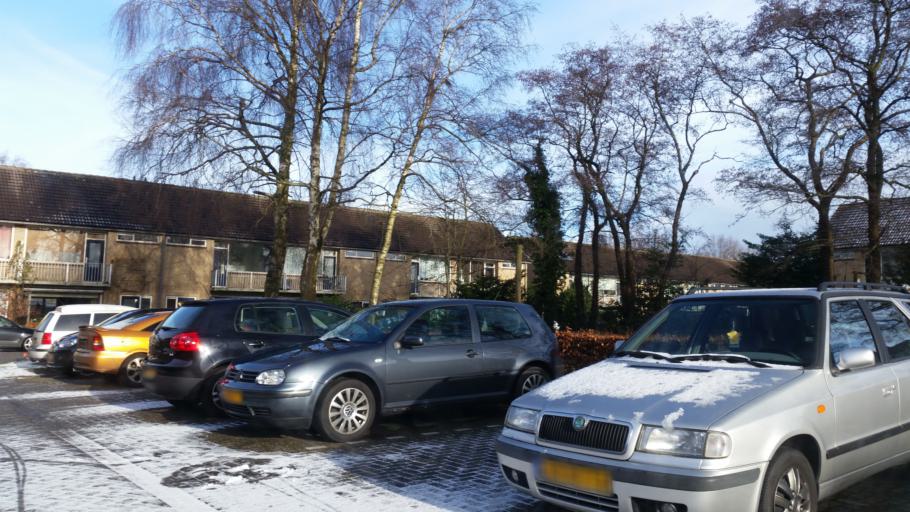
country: NL
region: Friesland
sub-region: Gemeente Tytsjerksteradiel
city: Burgum
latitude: 53.1990
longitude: 5.9963
